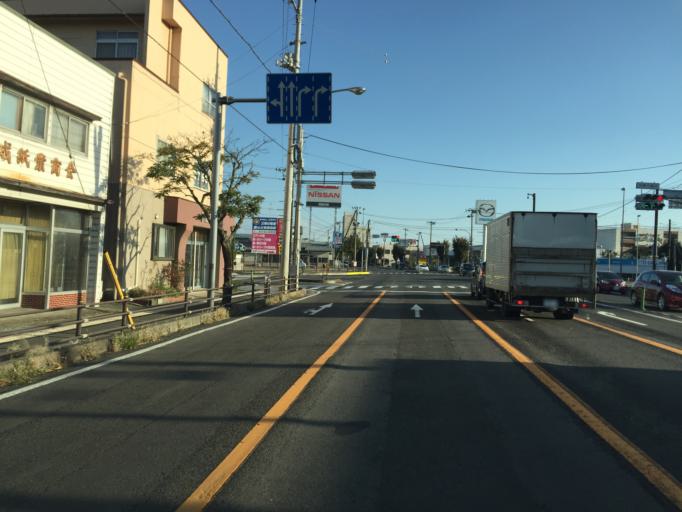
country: JP
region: Fukushima
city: Fukushima-shi
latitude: 37.7714
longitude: 140.4827
